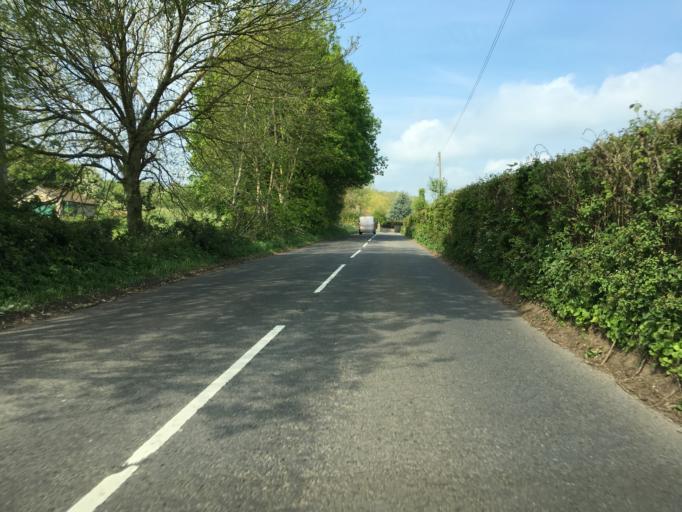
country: GB
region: England
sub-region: North Somerset
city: Winford
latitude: 51.3847
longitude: -2.6705
